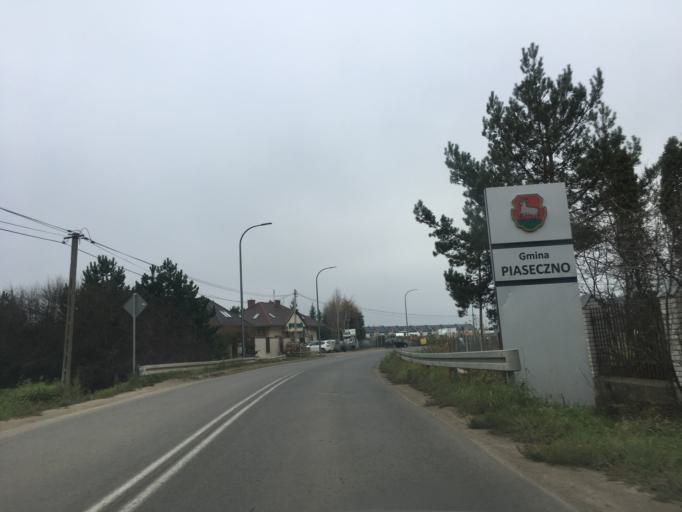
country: PL
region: Masovian Voivodeship
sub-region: Powiat piaseczynski
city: Lesznowola
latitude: 52.0722
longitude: 20.9666
